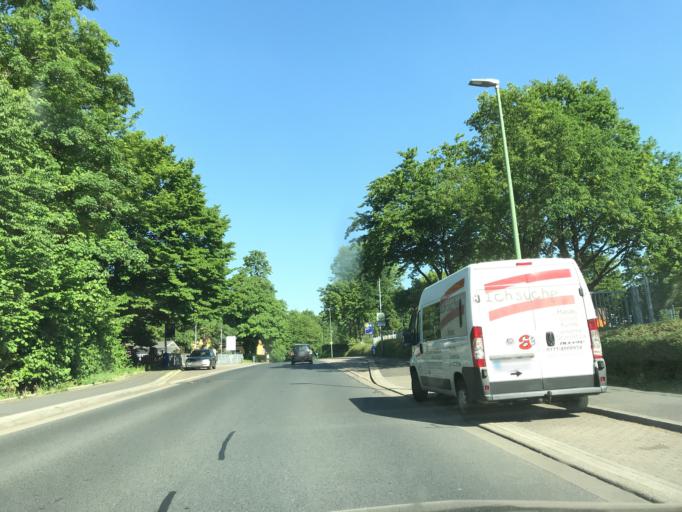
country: DE
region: North Rhine-Westphalia
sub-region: Regierungsbezirk Dusseldorf
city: Essen
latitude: 51.4736
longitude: 7.0594
